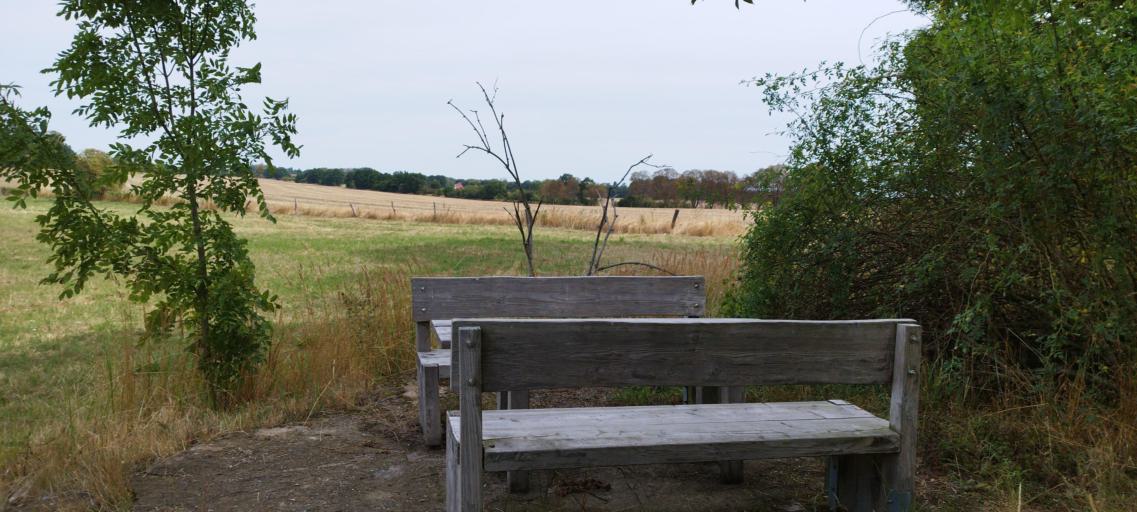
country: DE
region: Brandenburg
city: Wiesenburg
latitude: 52.1227
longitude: 12.5049
